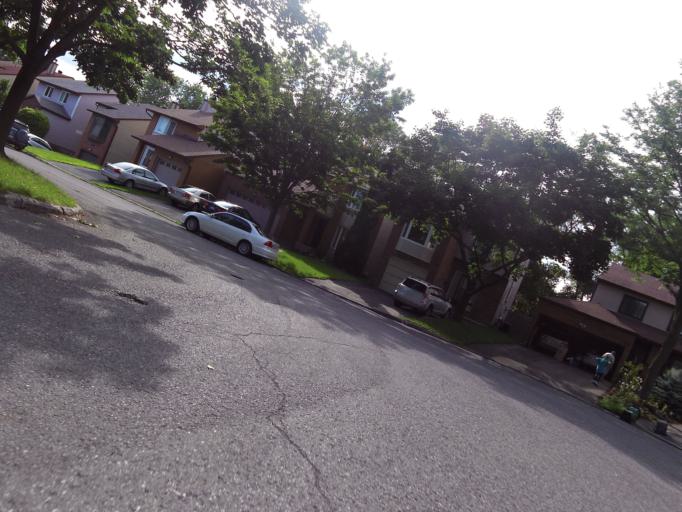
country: CA
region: Ontario
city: Bells Corners
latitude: 45.3505
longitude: -75.8000
